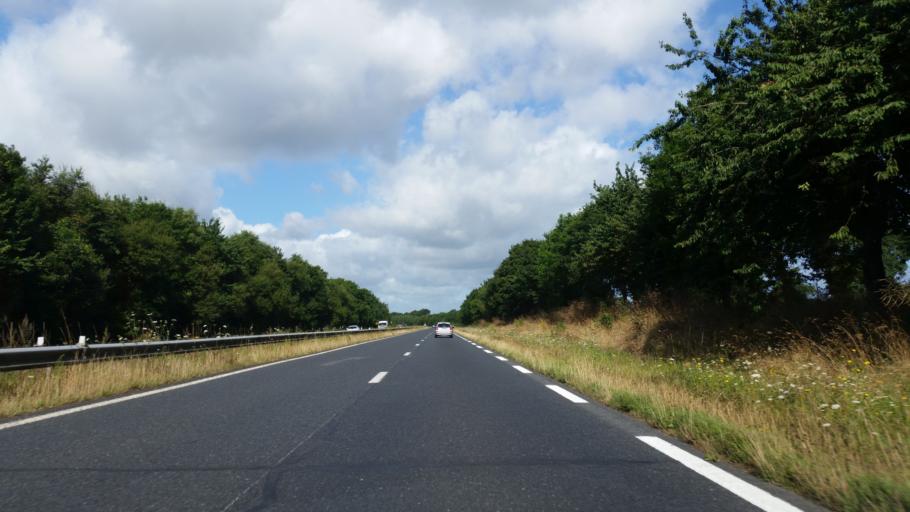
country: FR
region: Lower Normandy
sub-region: Departement du Calvados
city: Grandcamp-Maisy
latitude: 49.3416
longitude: -0.9490
